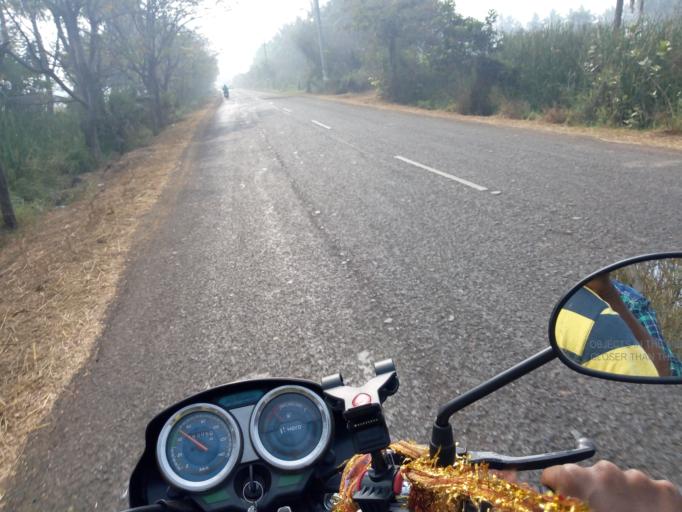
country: IN
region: Andhra Pradesh
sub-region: West Godavari
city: Tadepallegudem
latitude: 16.7943
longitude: 81.4165
